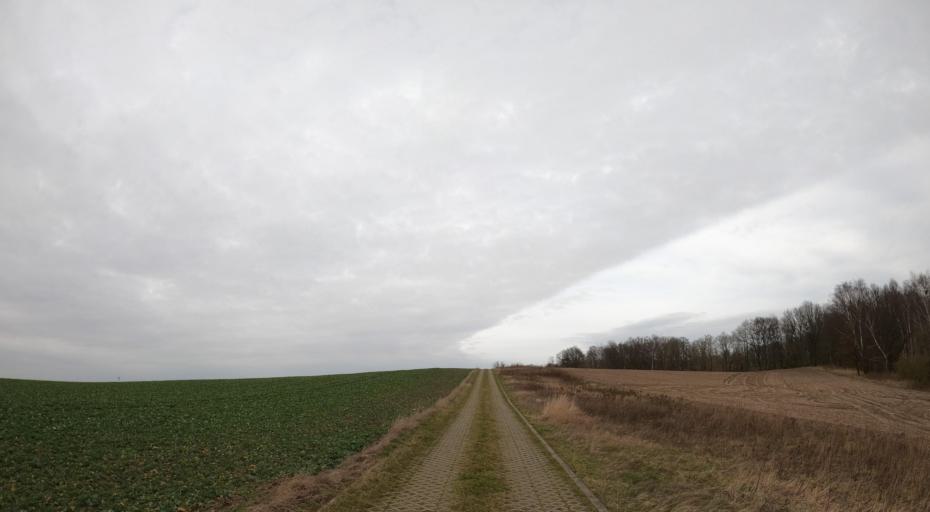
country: PL
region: West Pomeranian Voivodeship
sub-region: Powiat pyrzycki
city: Bielice
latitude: 53.2544
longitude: 14.6393
